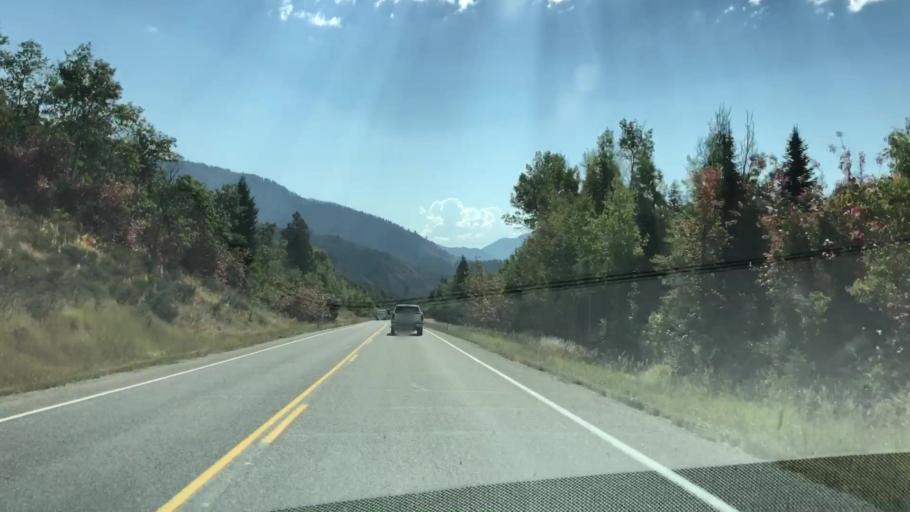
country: US
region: Wyoming
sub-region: Teton County
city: Hoback
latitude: 43.2273
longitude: -111.0850
